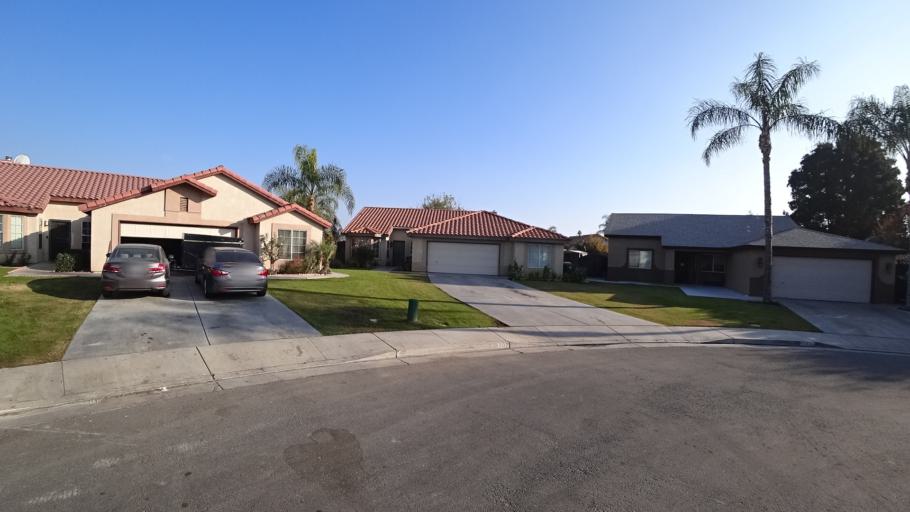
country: US
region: California
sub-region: Kern County
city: Greenfield
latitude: 35.2878
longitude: -119.0058
